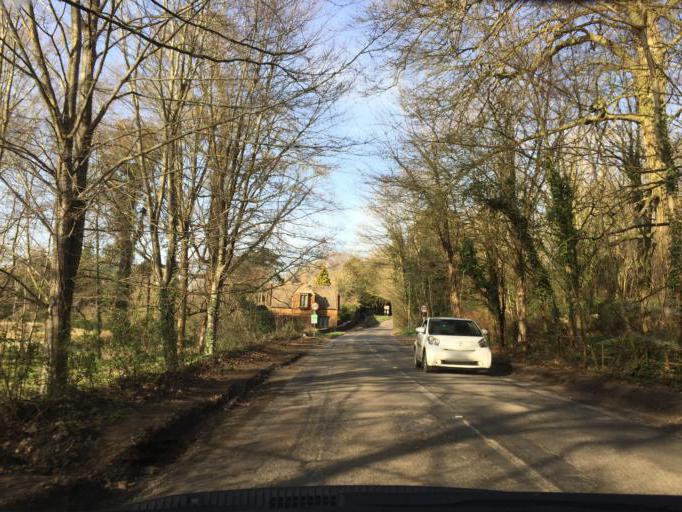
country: GB
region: England
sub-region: Oxfordshire
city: Bloxham
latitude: 52.0408
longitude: -1.3897
